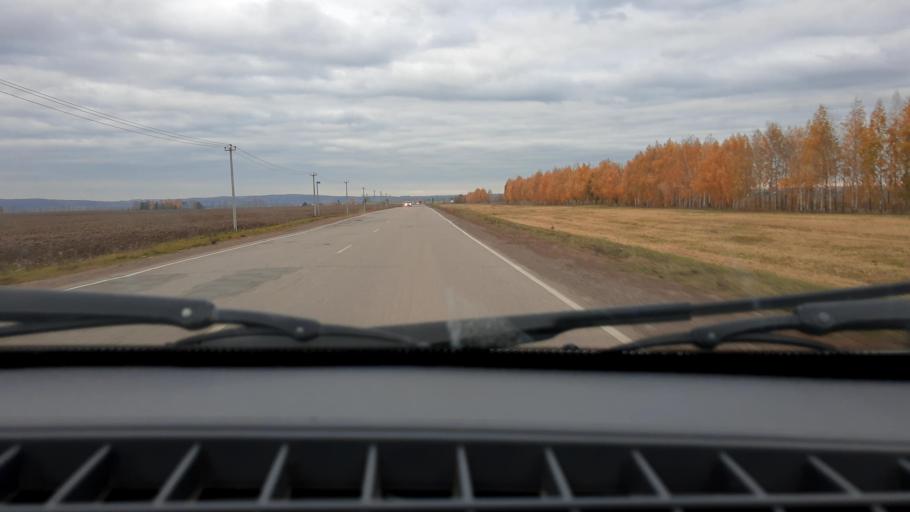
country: RU
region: Bashkortostan
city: Kabakovo
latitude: 54.5398
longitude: 56.0755
